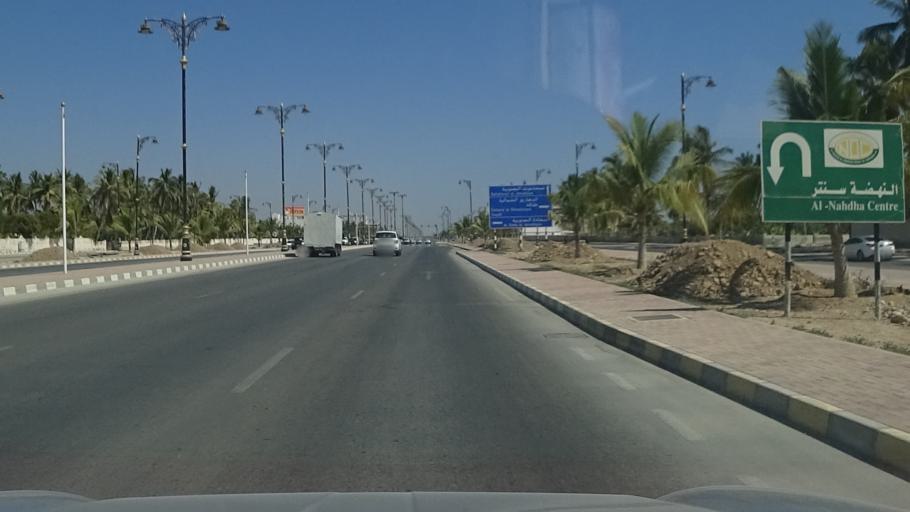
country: OM
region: Zufar
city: Salalah
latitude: 17.0362
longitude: 54.1569
